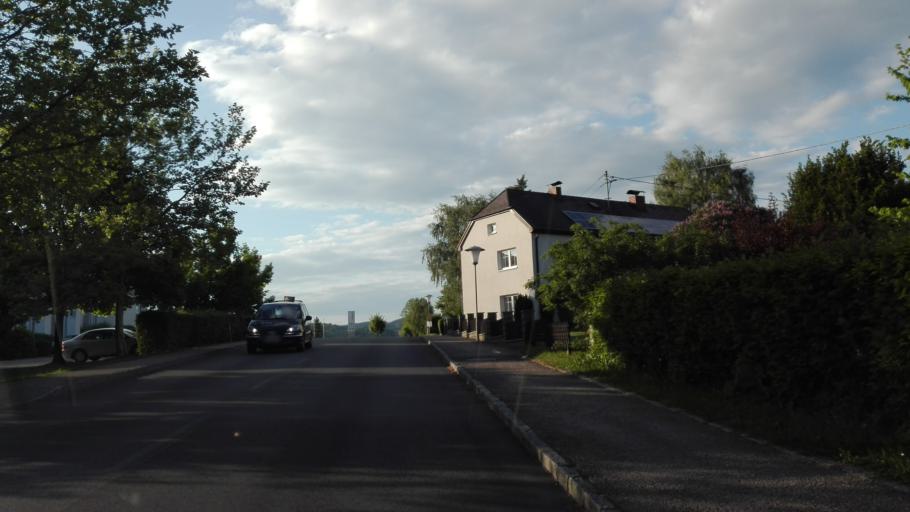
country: AT
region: Upper Austria
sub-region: Politischer Bezirk Urfahr-Umgebung
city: Engerwitzdorf
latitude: 48.3687
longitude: 14.5152
